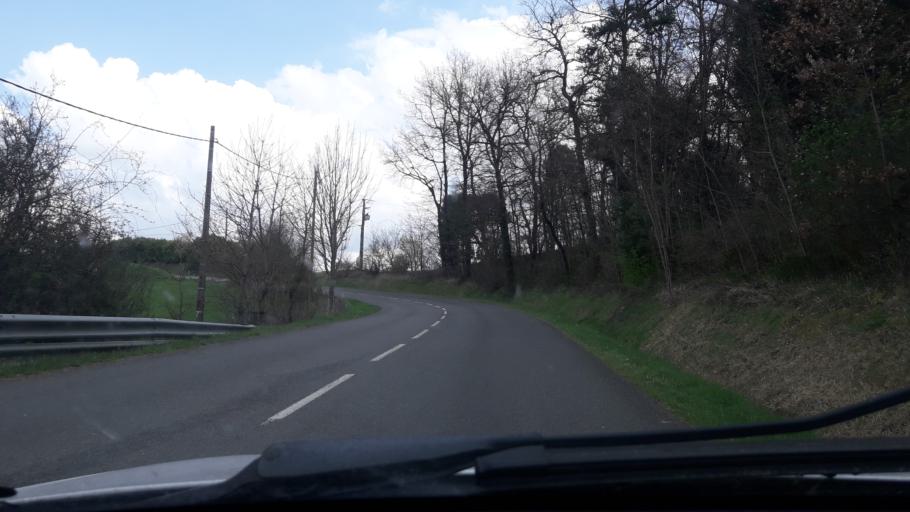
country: FR
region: Midi-Pyrenees
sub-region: Departement de la Haute-Garonne
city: Montesquieu-Volvestre
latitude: 43.2131
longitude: 1.2349
